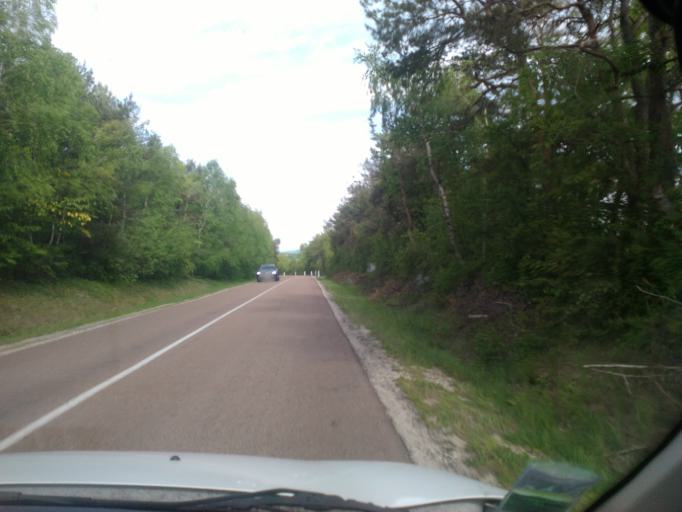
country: FR
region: Champagne-Ardenne
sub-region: Departement de l'Aube
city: Payns
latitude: 48.3820
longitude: 3.8670
